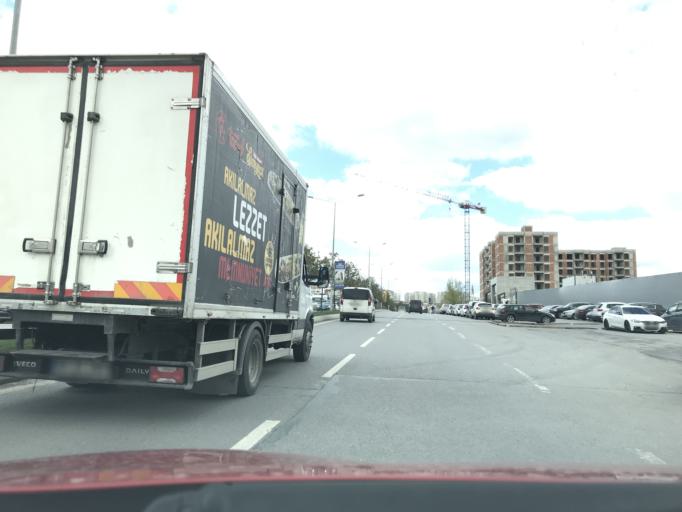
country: TR
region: Istanbul
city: Sultanbeyli
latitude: 40.9294
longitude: 29.3085
